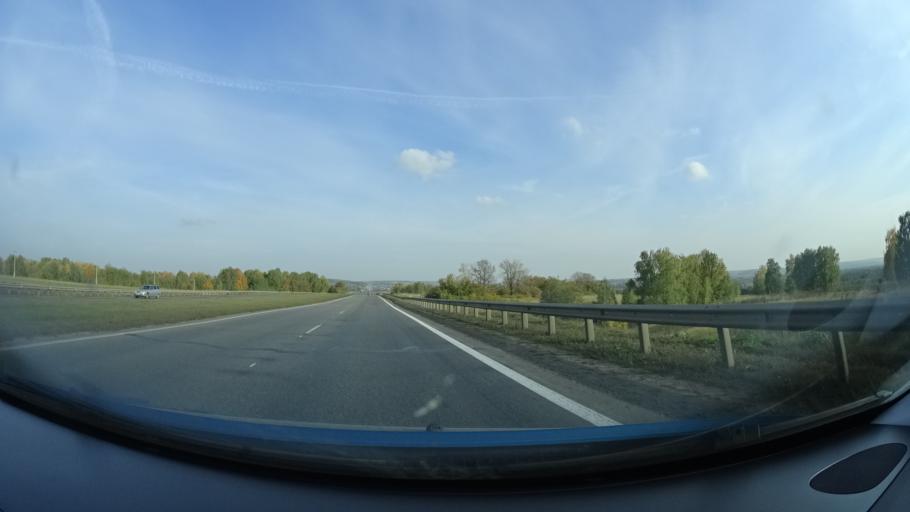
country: RU
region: Bashkortostan
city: Chishmy
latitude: 54.6512
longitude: 55.5118
